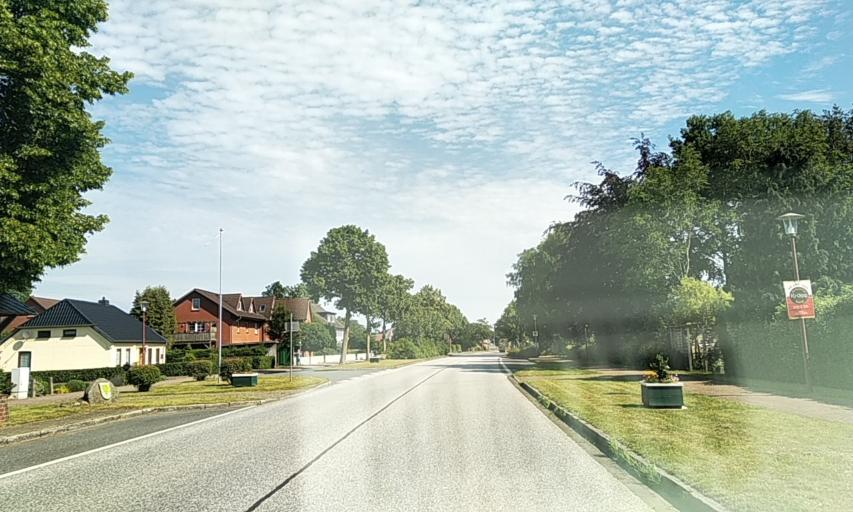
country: DE
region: Schleswig-Holstein
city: Jagel
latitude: 54.4547
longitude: 9.5370
